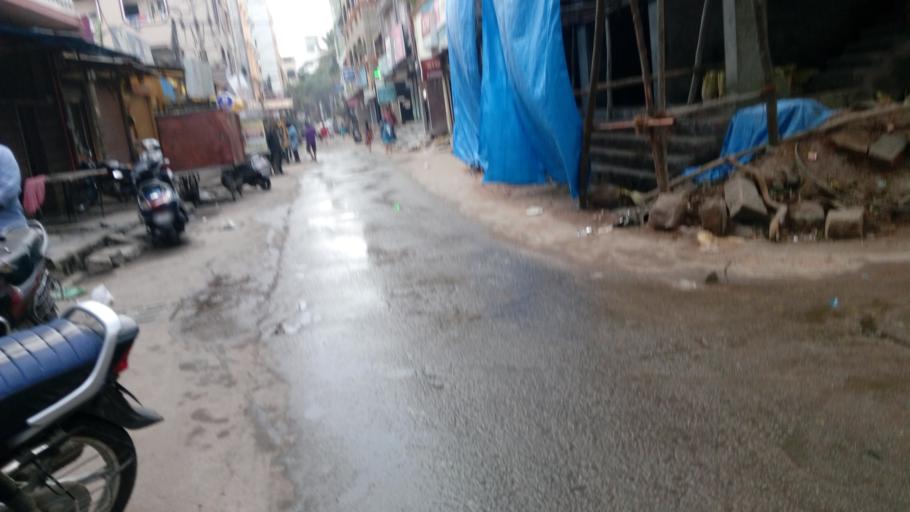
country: IN
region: Telangana
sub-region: Rangareddi
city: Kukatpalli
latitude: 17.4411
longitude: 78.4475
